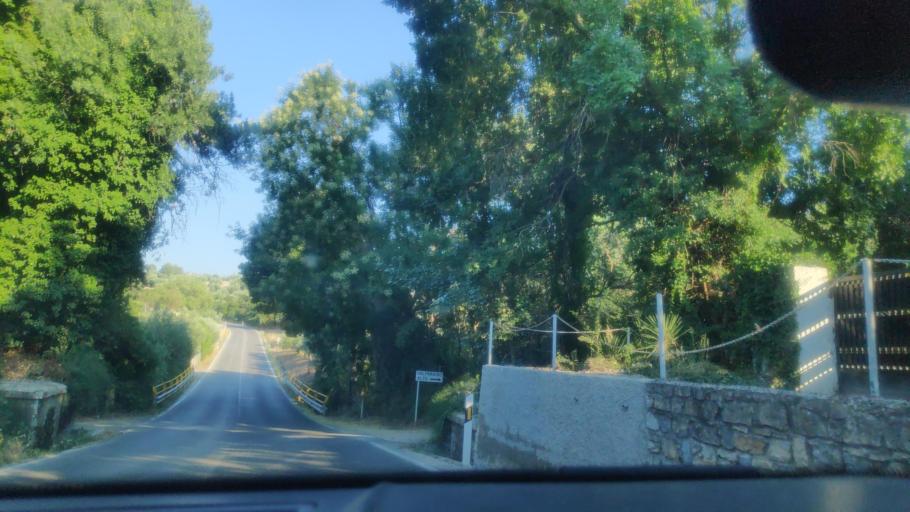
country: ES
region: Andalusia
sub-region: Provincia de Jaen
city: Jaen
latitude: 37.7495
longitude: -3.7944
